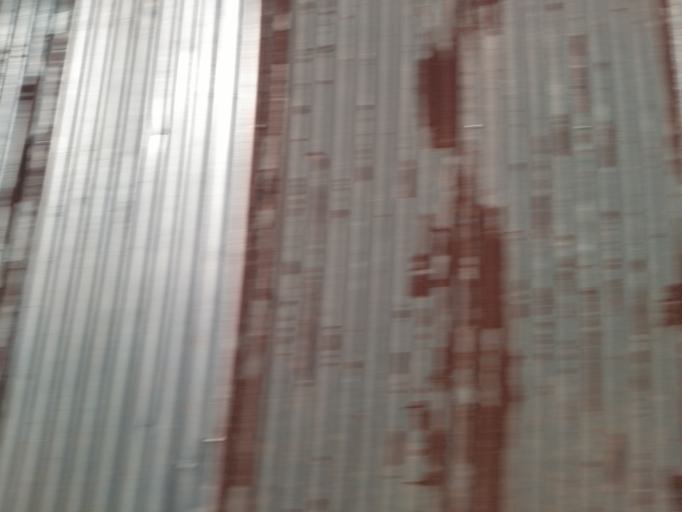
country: TZ
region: Dar es Salaam
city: Magomeni
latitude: -6.7475
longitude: 39.2406
